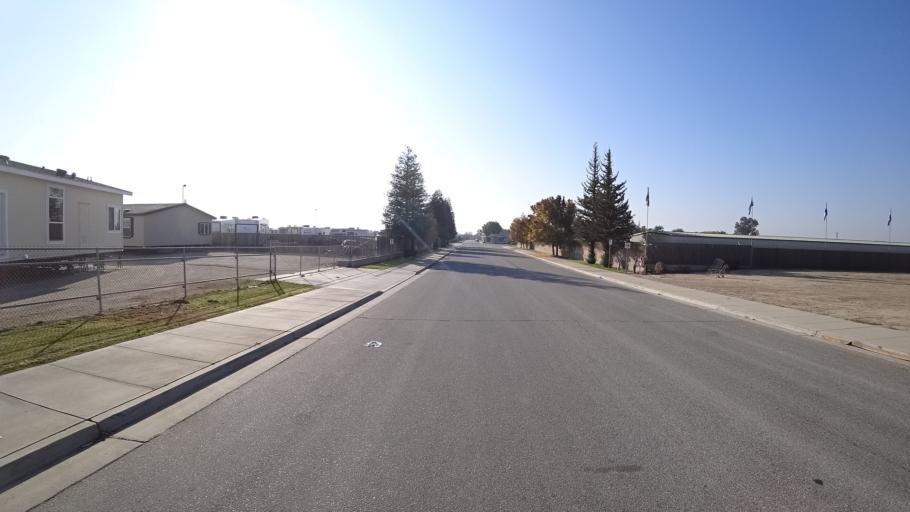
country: US
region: California
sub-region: Kern County
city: Greenfield
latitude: 35.2665
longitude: -119.0191
